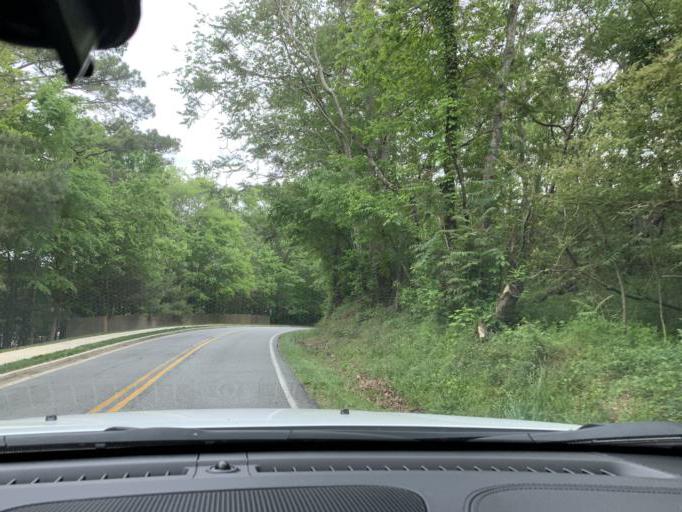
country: US
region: Georgia
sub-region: Gwinnett County
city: Suwanee
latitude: 34.1150
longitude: -84.1130
